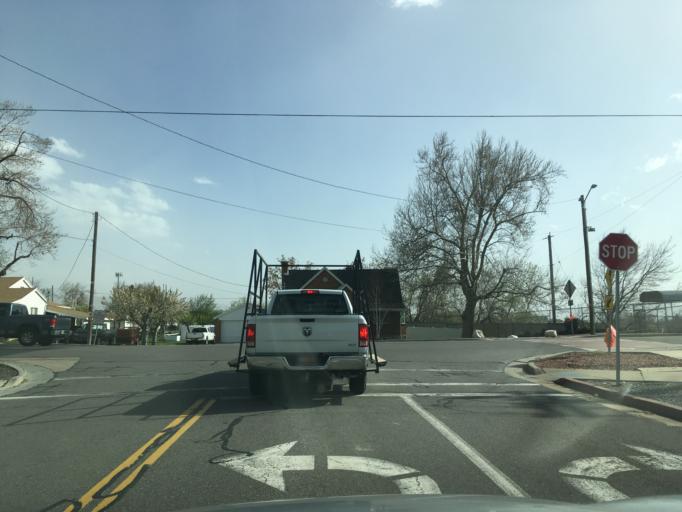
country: US
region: Utah
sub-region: Davis County
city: Farmington
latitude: 40.9808
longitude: -111.8962
